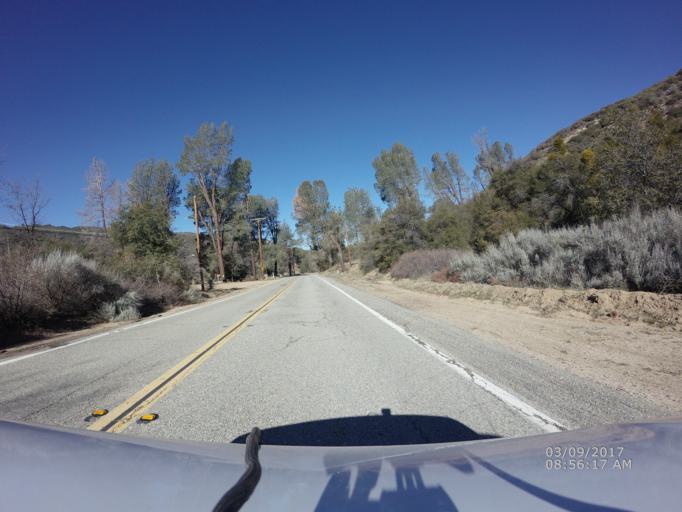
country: US
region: California
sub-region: Los Angeles County
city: Green Valley
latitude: 34.7174
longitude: -118.5757
